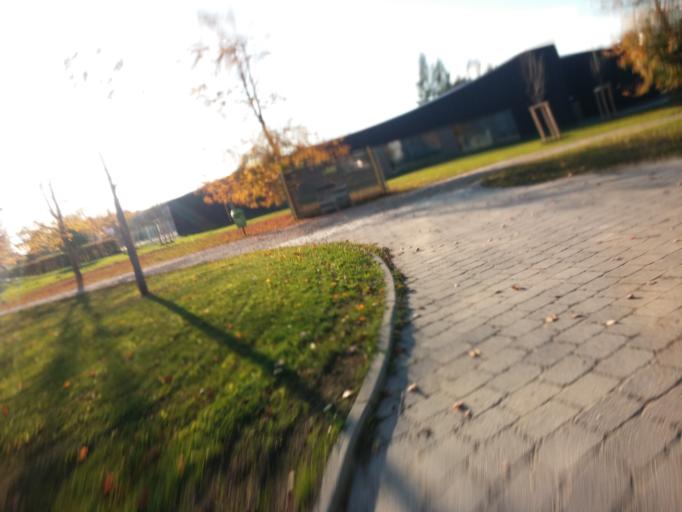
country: DE
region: Bavaria
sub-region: Upper Bavaria
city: Vaterstetten
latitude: 48.0978
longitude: 11.7905
